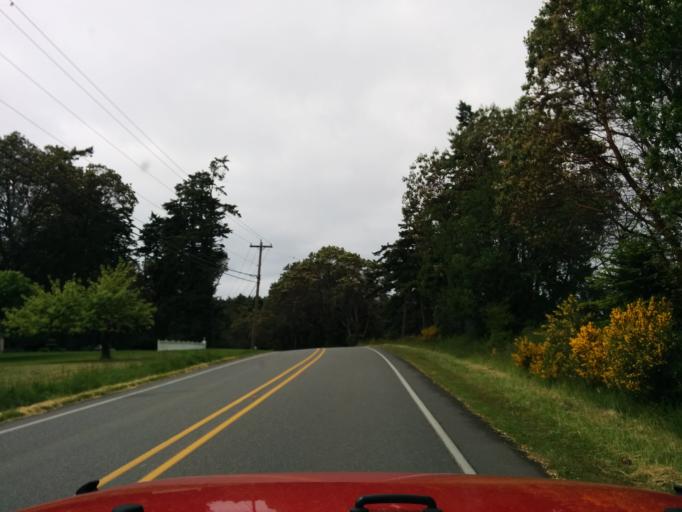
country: US
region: Washington
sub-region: Island County
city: Coupeville
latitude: 48.2144
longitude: -122.7156
